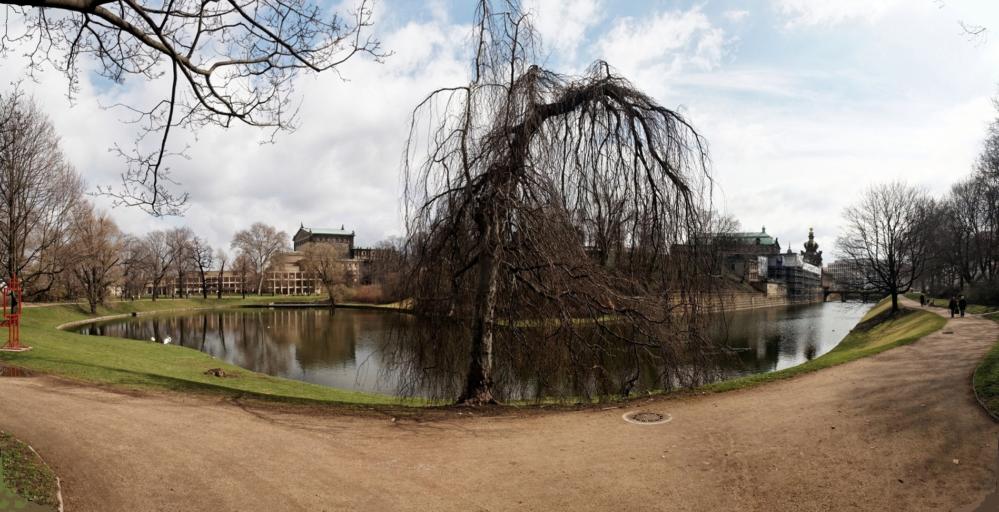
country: DE
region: Saxony
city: Dresden
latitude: 51.0541
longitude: 13.7312
